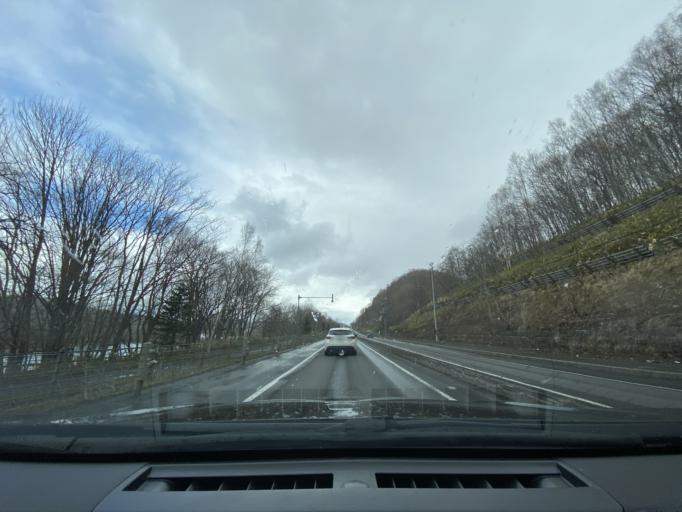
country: JP
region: Hokkaido
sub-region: Asahikawa-shi
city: Asahikawa
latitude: 43.7567
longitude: 142.2753
